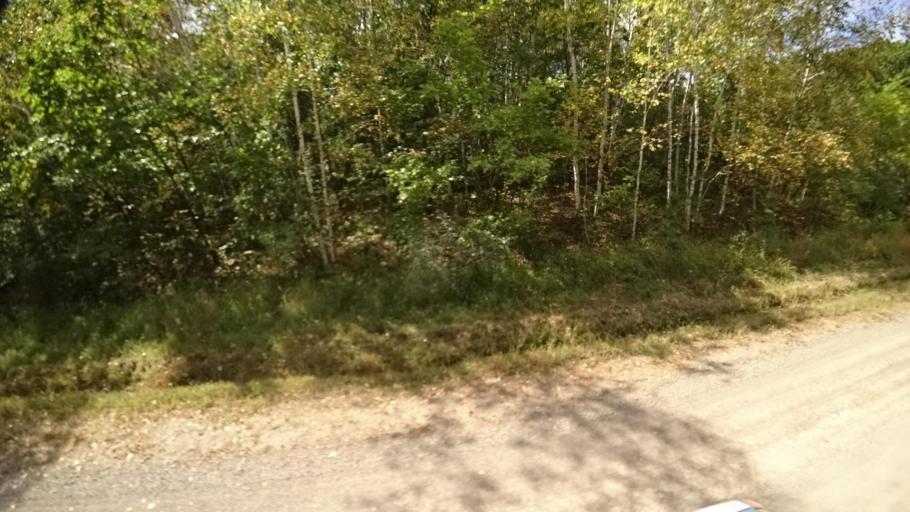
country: RU
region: Primorskiy
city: Yakovlevka
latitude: 44.7010
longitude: 133.6434
